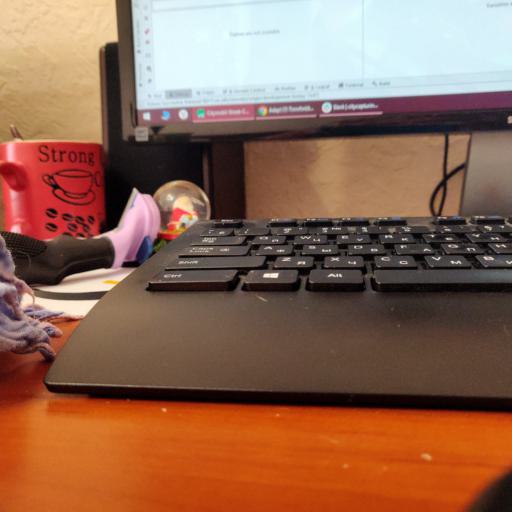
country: FI
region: Haeme
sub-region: Forssa
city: Humppila
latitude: 60.8930
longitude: 23.4327
